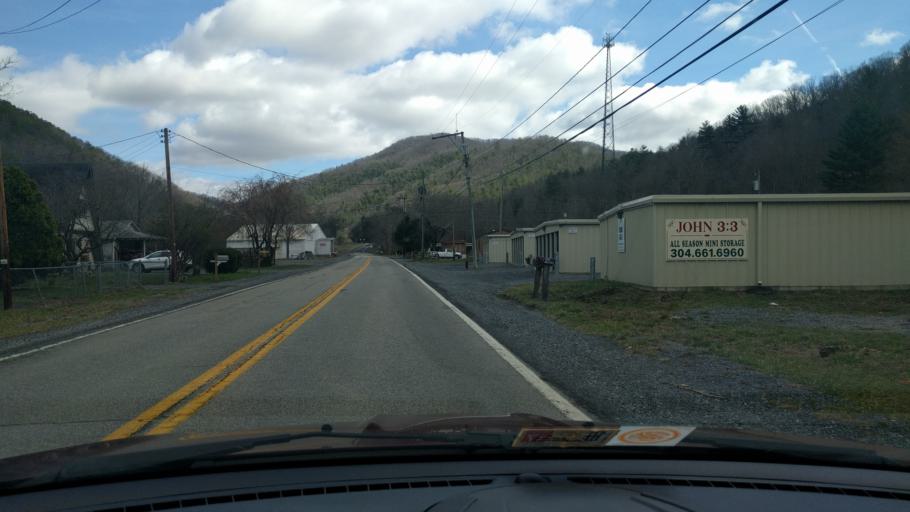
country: US
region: West Virginia
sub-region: Greenbrier County
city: White Sulphur Springs
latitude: 37.7940
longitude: -80.2748
